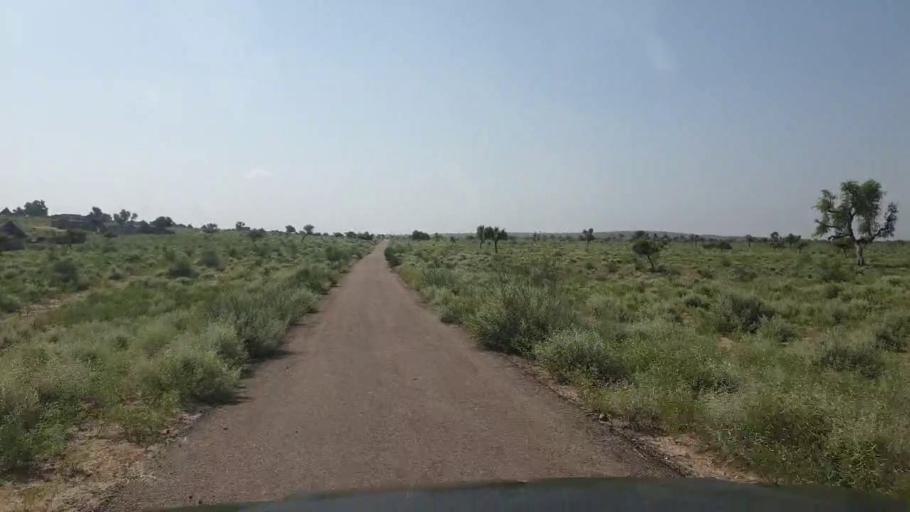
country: PK
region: Sindh
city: Islamkot
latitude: 25.1855
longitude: 70.3920
